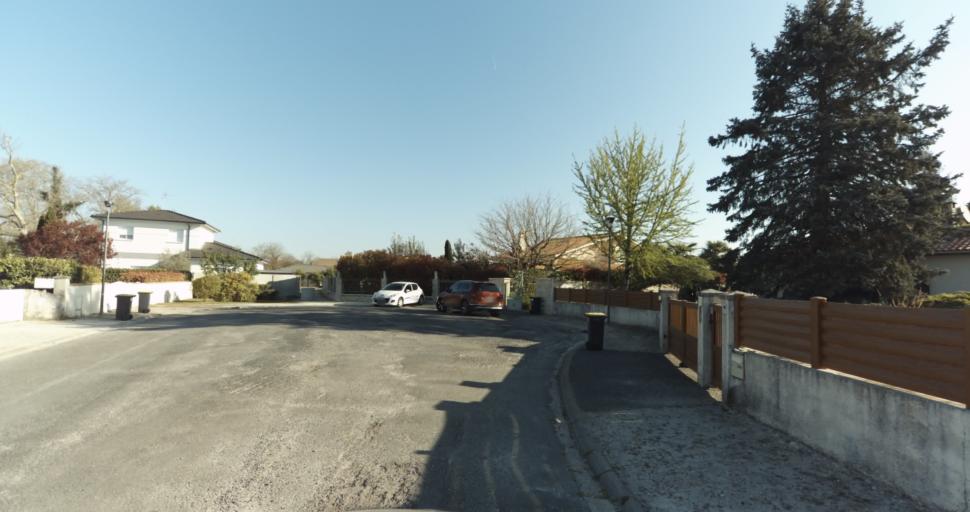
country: FR
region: Aquitaine
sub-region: Departement de la Gironde
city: Martignas-sur-Jalle
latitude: 44.8112
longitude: -0.7869
